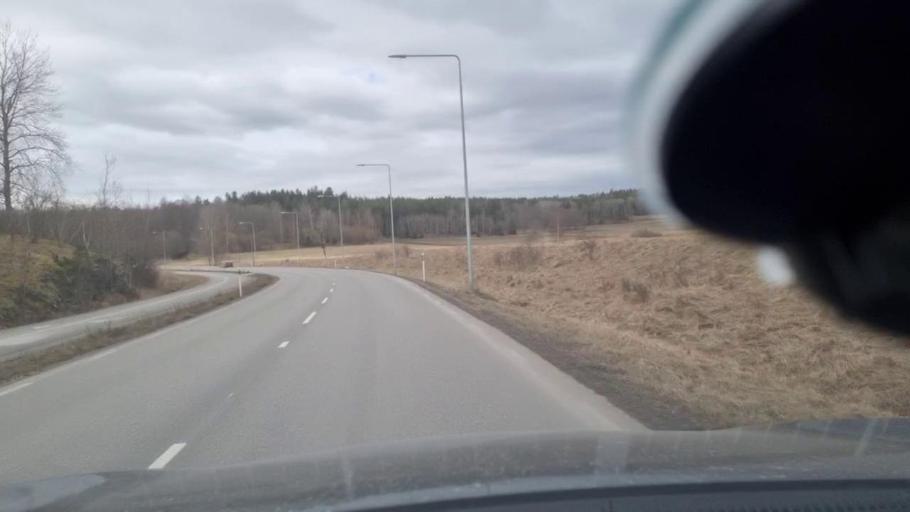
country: SE
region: Stockholm
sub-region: Jarfalla Kommun
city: Jakobsberg
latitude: 59.4268
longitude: 17.7940
